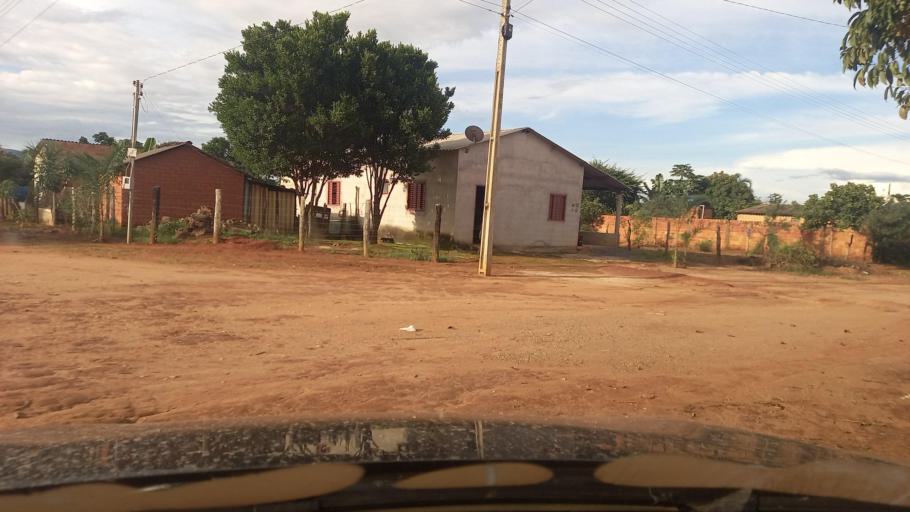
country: BR
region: Goias
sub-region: Cavalcante
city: Cavalcante
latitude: -13.8010
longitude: -47.4448
